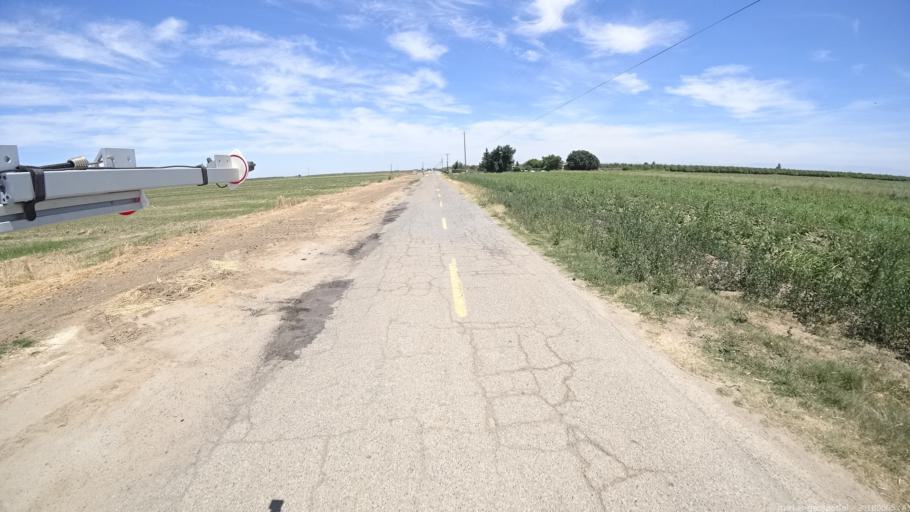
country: US
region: California
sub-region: Madera County
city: Chowchilla
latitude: 37.0870
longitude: -120.3651
